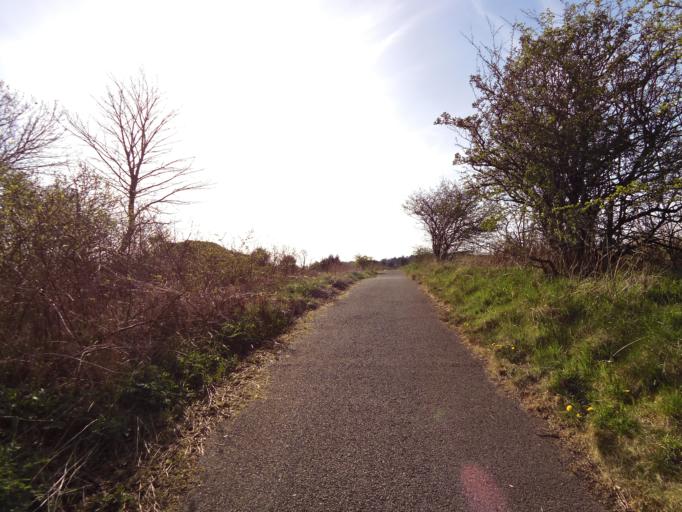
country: GB
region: Scotland
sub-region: Fife
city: Tayport
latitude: 56.4816
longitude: -2.8066
